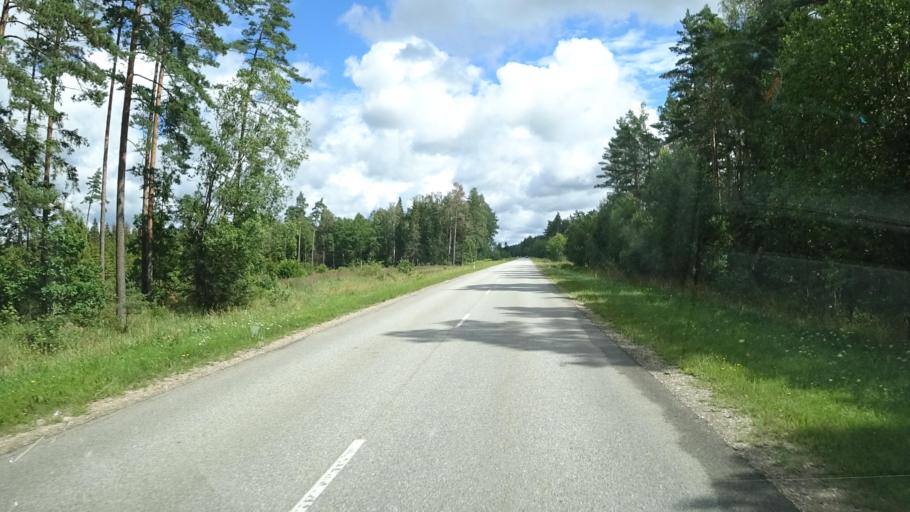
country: LV
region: Pavilostas
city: Pavilosta
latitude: 56.7309
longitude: 21.2082
